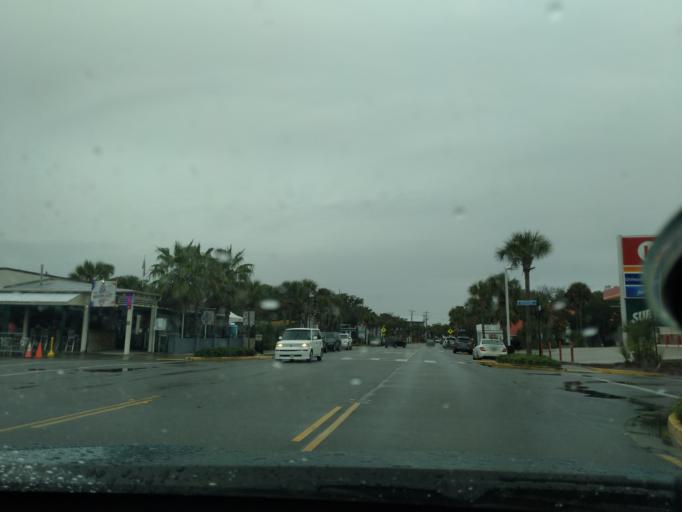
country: US
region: South Carolina
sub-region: Charleston County
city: Folly Beach
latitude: 32.6568
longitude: -79.9415
